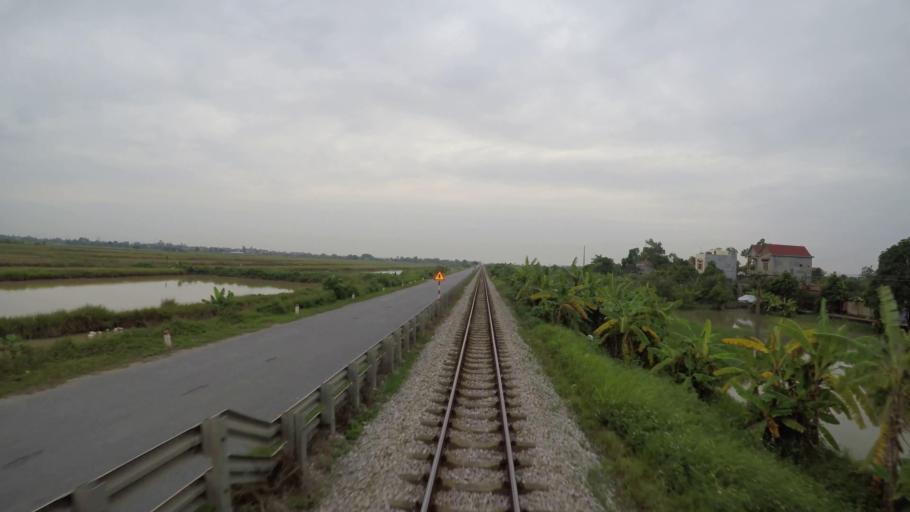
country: VN
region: Hung Yen
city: Ban Yen Nhan
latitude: 20.9790
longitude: 106.0832
